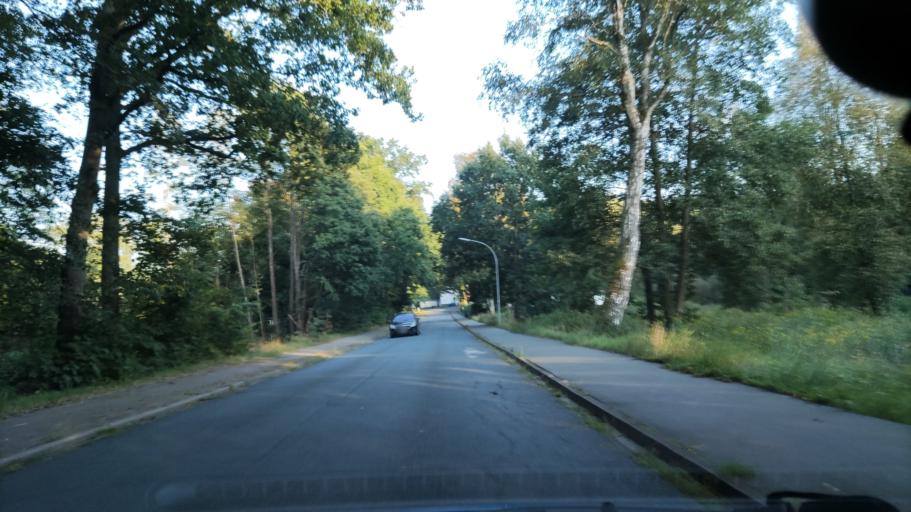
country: DE
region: Lower Saxony
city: Fassberg
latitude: 52.9627
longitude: 10.1809
